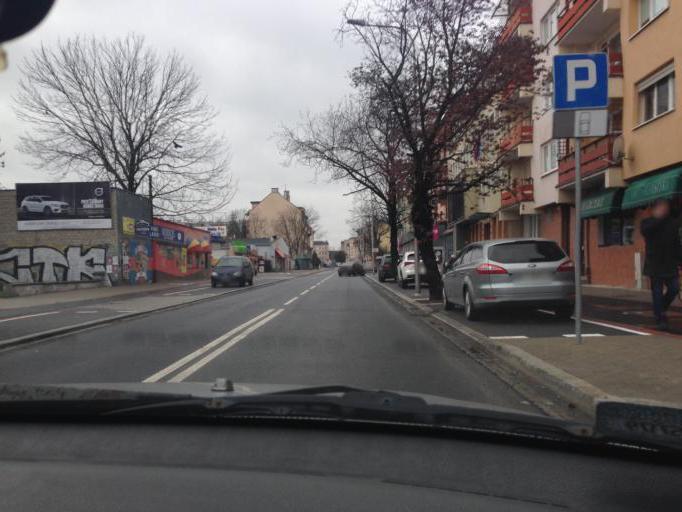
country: PL
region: Opole Voivodeship
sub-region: Powiat opolski
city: Opole
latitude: 50.6729
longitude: 17.9292
